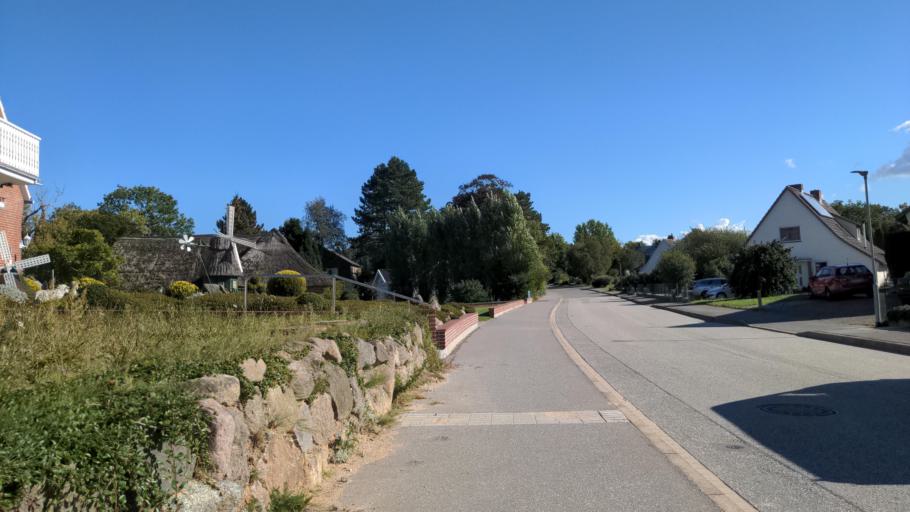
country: DE
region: Schleswig-Holstein
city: Beschendorf
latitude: 54.1638
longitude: 10.8860
